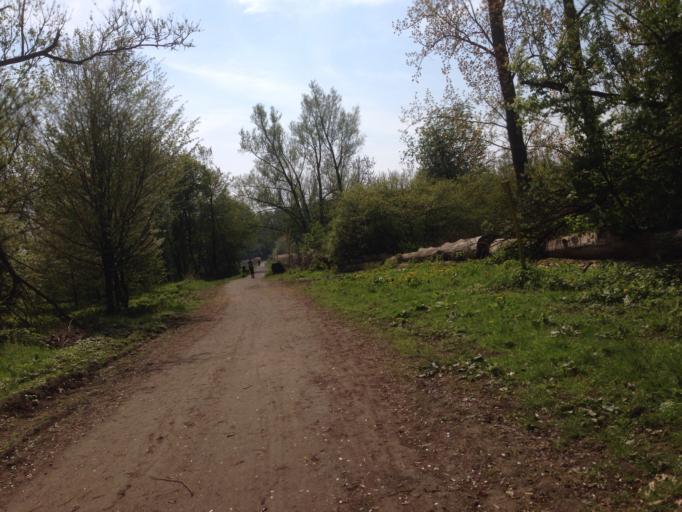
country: DE
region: Hesse
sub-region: Regierungsbezirk Giessen
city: Giessen
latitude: 50.5971
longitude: 8.6984
